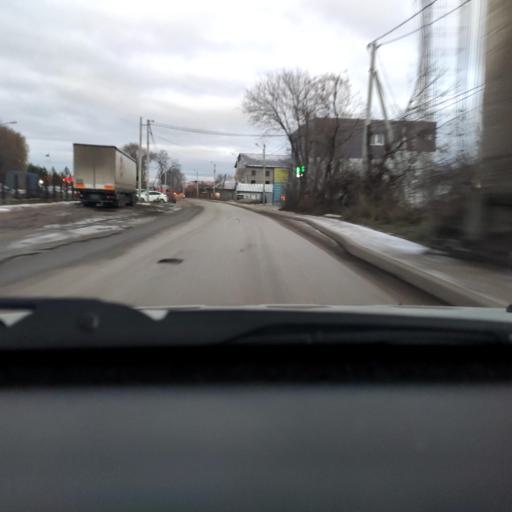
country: RU
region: Perm
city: Kondratovo
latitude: 57.9525
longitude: 56.1371
